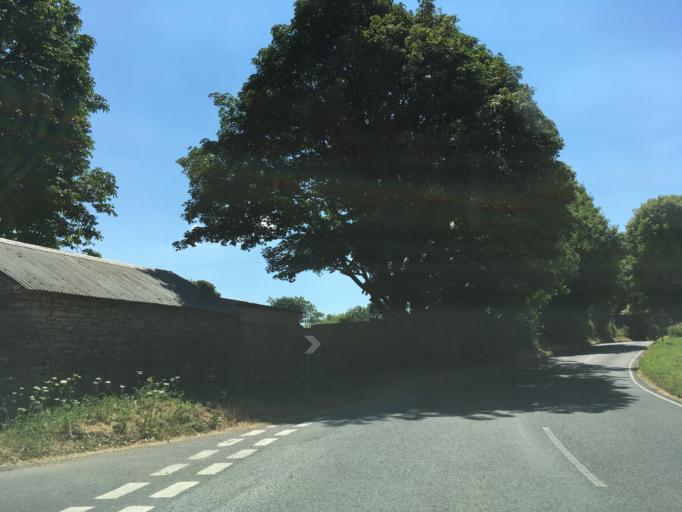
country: GB
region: England
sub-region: Gloucestershire
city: Chalford
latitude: 51.7473
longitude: -2.1380
